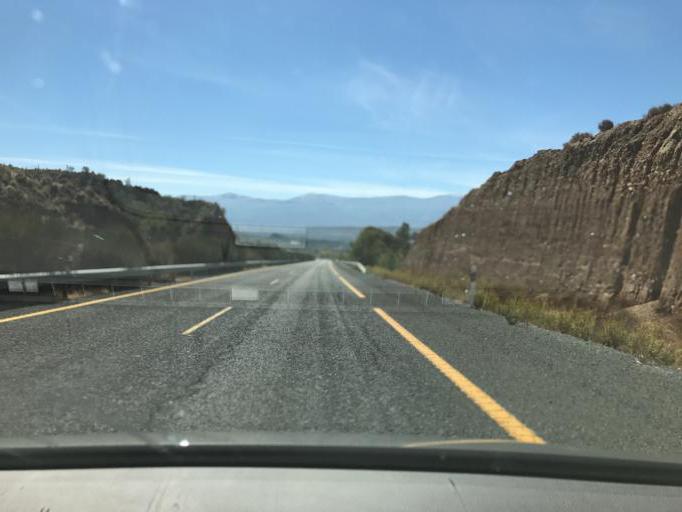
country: ES
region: Andalusia
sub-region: Provincia de Granada
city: Guadix
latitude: 37.3137
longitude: -3.1122
